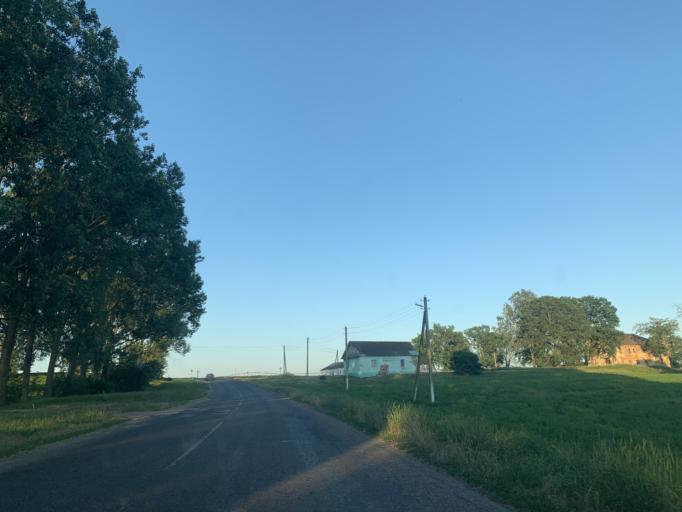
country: BY
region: Minsk
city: Haradzyeya
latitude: 53.2430
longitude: 26.5028
